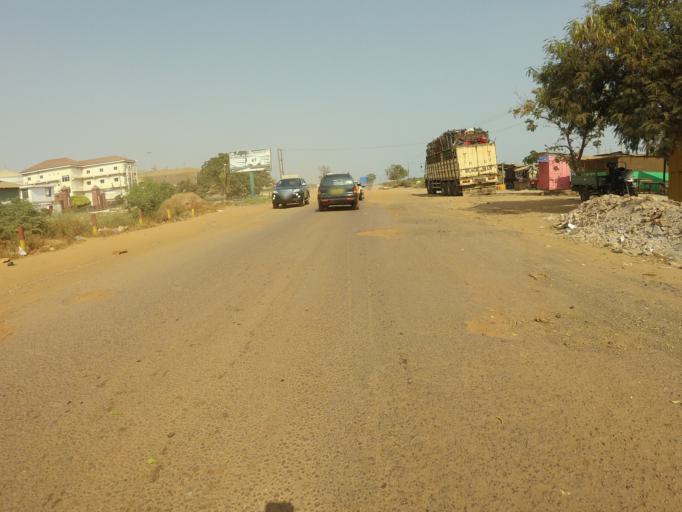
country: GH
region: Greater Accra
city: Tema
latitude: 5.6692
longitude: 0.0155
